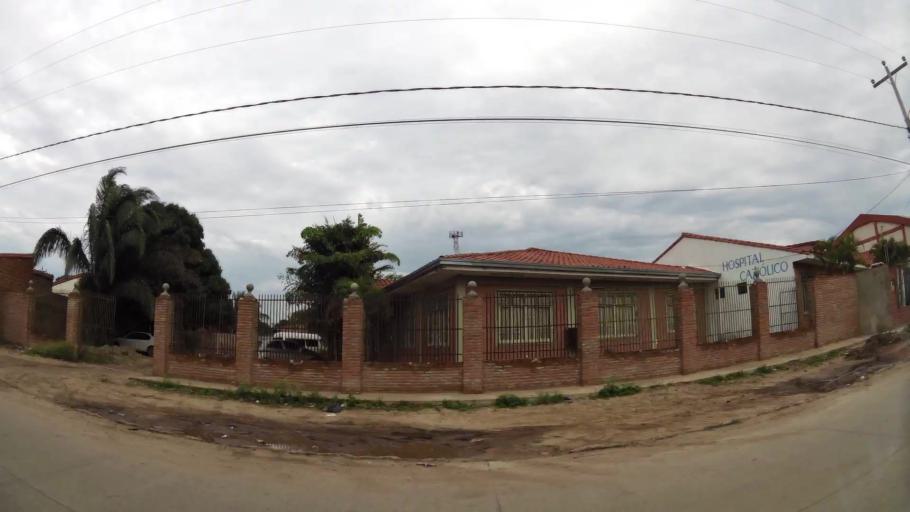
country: BO
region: Santa Cruz
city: Santa Cruz de la Sierra
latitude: -17.7364
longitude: -63.1612
